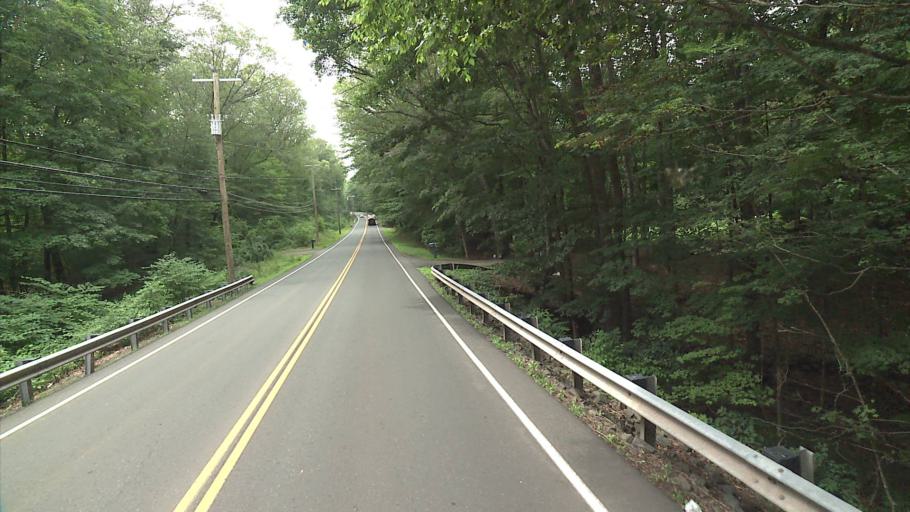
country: US
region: Connecticut
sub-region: New Haven County
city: Madison Center
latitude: 41.3601
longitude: -72.6292
